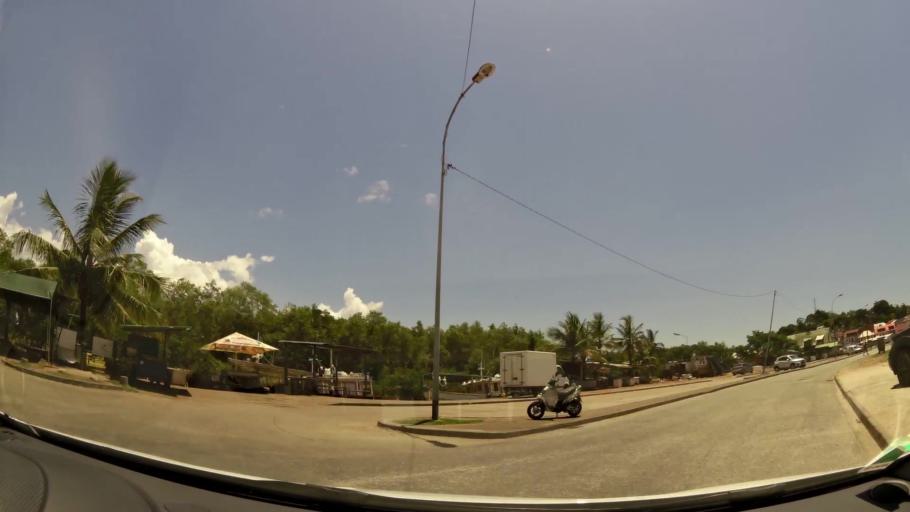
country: GF
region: Guyane
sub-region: Guyane
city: Cayenne
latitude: 4.9336
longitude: -52.3346
